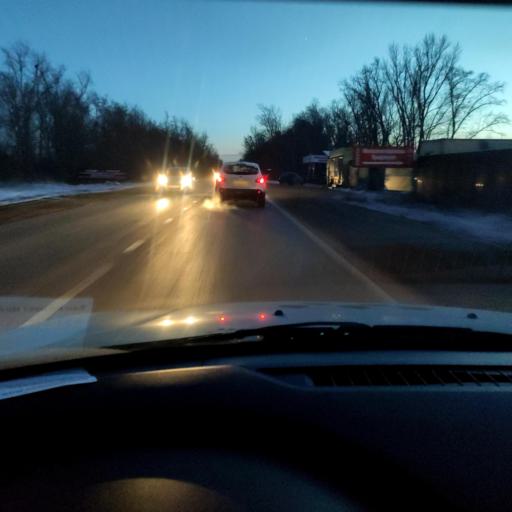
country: RU
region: Samara
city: Tol'yatti
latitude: 53.5545
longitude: 49.3939
